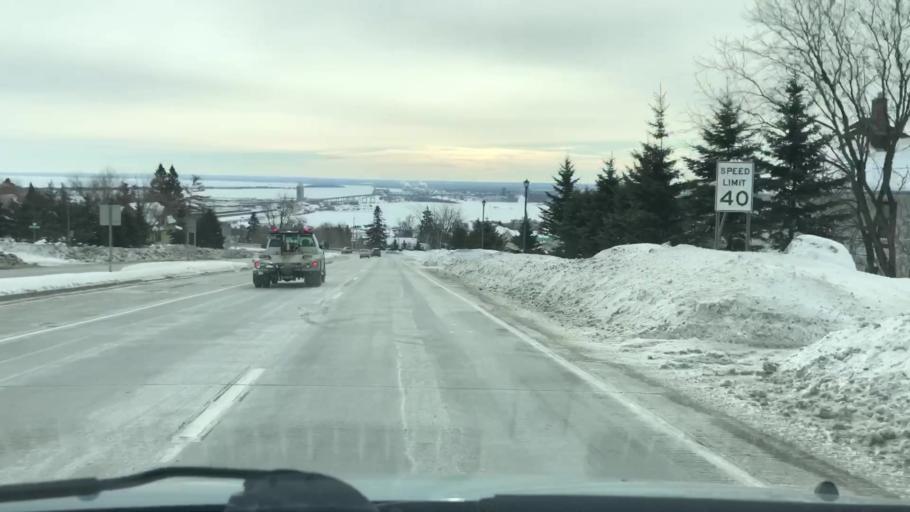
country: US
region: Minnesota
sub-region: Saint Louis County
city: Duluth
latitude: 46.7726
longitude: -92.1393
